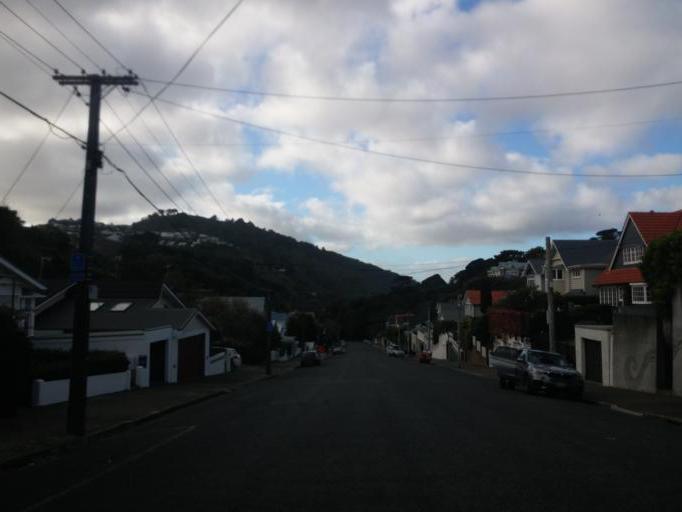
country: NZ
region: Wellington
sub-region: Wellington City
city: Kelburn
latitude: -41.2876
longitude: 174.7633
